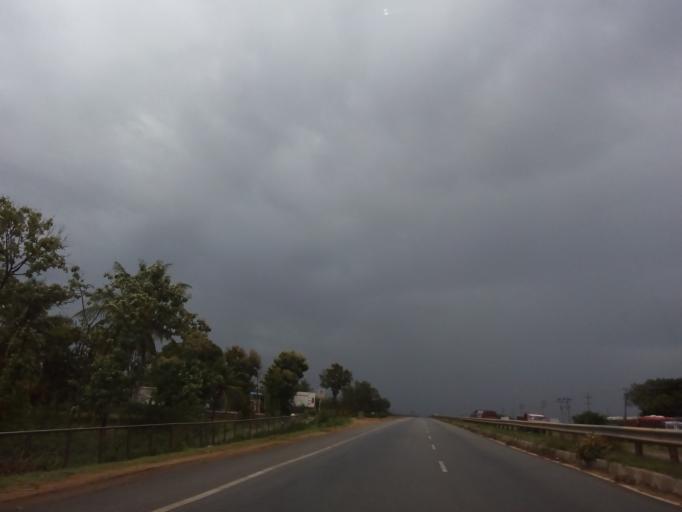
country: IN
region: Karnataka
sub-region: Davanagere
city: Harihar
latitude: 14.4475
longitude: 75.8850
